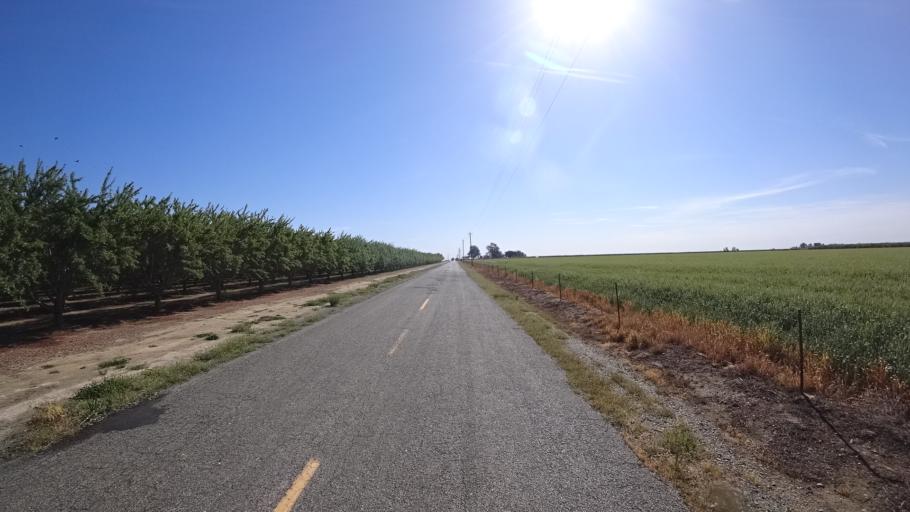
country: US
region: California
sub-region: Glenn County
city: Willows
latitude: 39.6113
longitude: -122.1630
